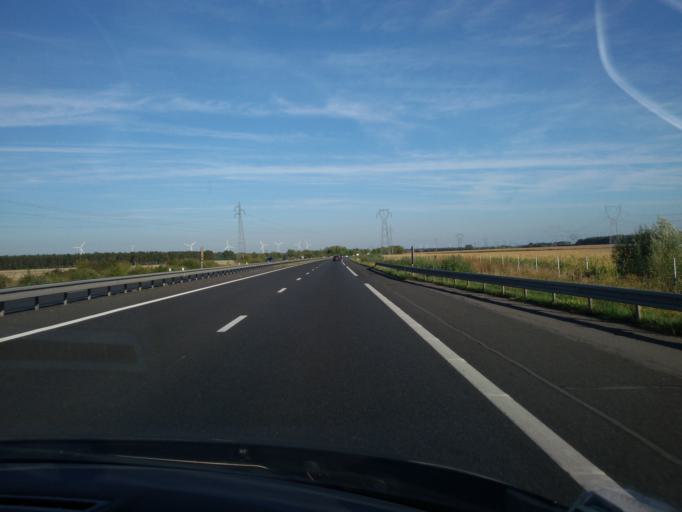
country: FR
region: Centre
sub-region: Departement du Cher
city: Marmagne
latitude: 47.0666
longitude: 2.2902
